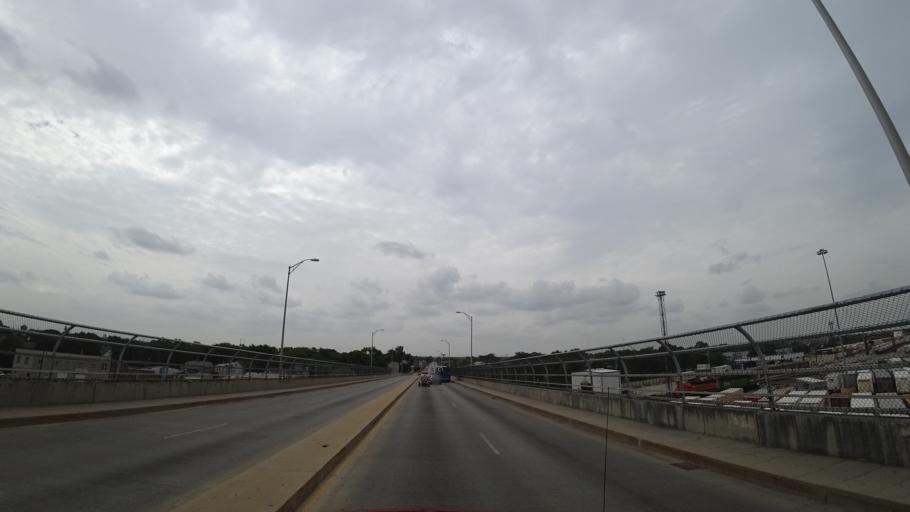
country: US
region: Illinois
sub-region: Cook County
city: Cicero
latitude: 41.8420
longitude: -87.7538
